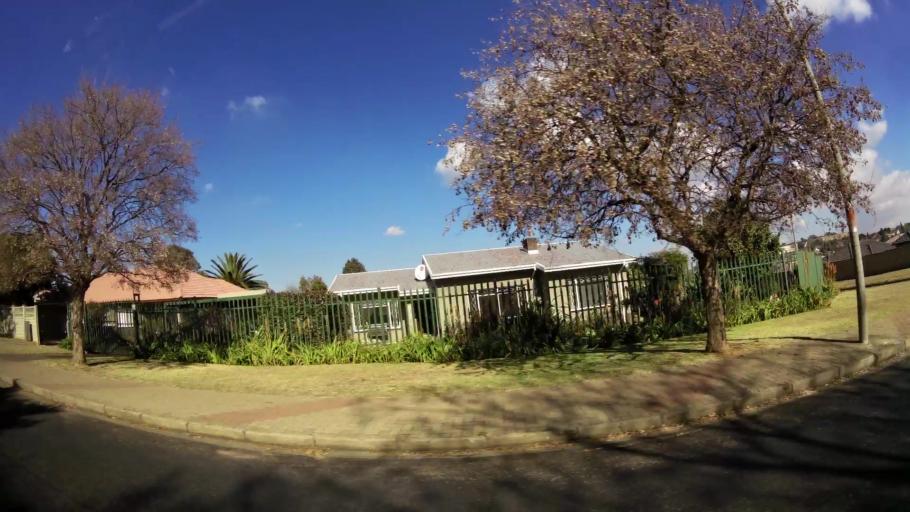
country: ZA
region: Gauteng
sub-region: City of Johannesburg Metropolitan Municipality
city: Roodepoort
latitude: -26.1411
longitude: 27.8248
